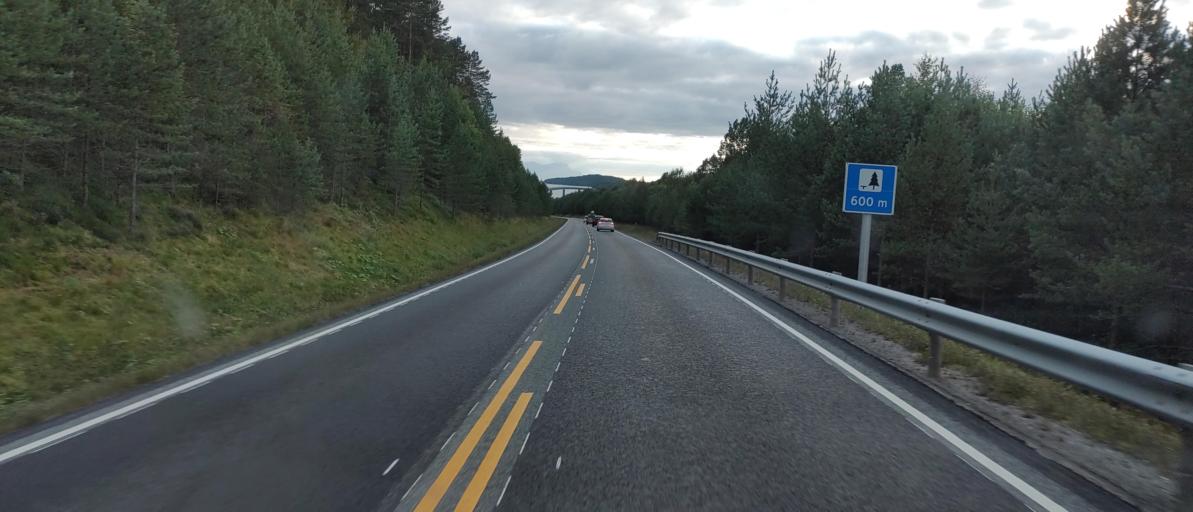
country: NO
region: More og Romsdal
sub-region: Molde
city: Hjelset
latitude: 62.7346
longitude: 7.3831
